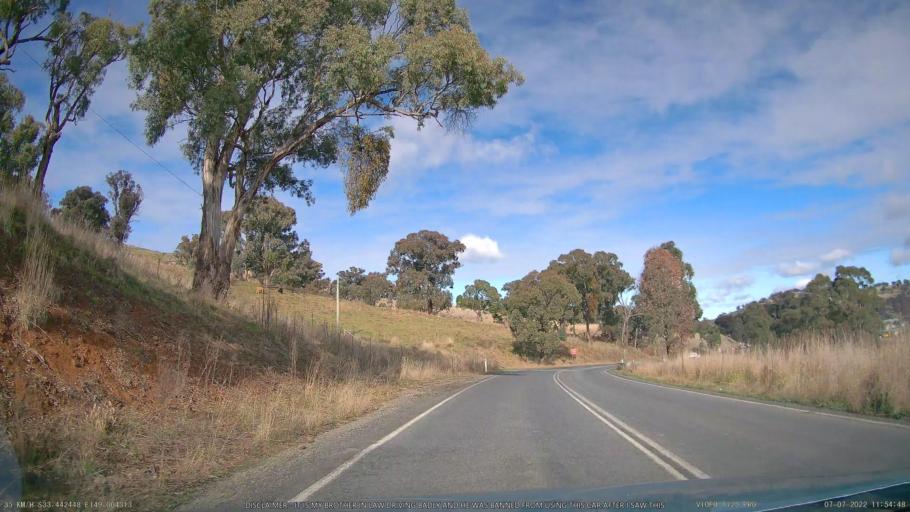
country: AU
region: New South Wales
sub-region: Blayney
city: Millthorpe
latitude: -33.4427
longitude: 149.0042
